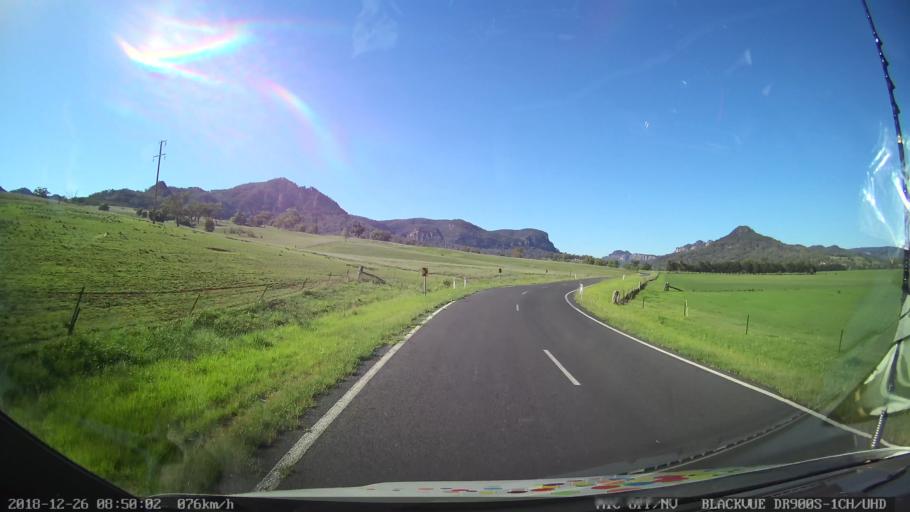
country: AU
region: New South Wales
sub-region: Mid-Western Regional
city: Kandos
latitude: -32.5712
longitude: 150.0972
